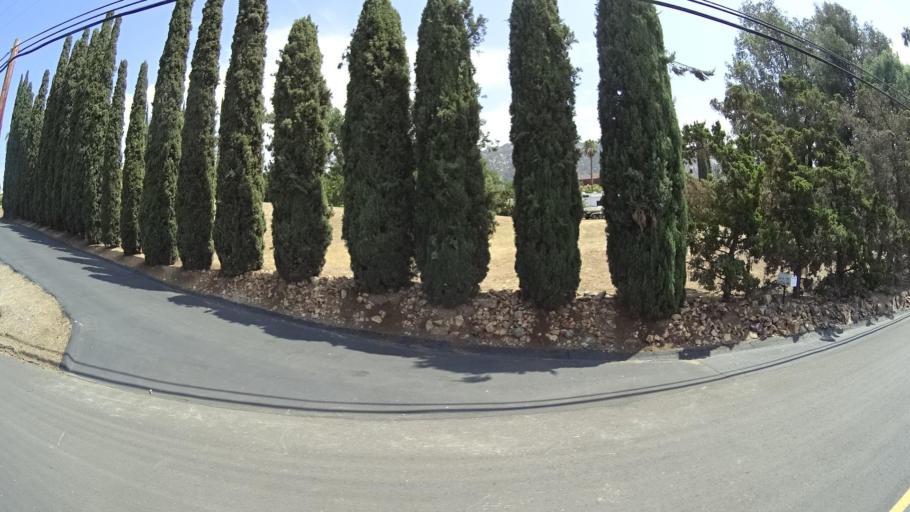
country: US
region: California
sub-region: San Diego County
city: Hidden Meadows
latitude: 33.1776
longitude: -117.0845
